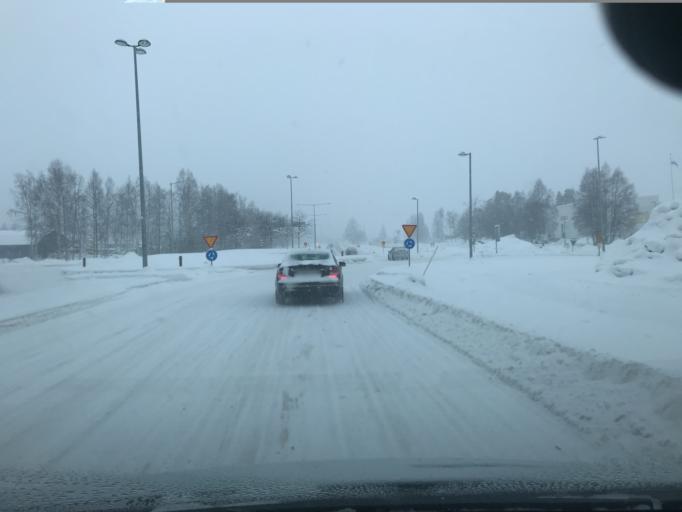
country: SE
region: Norrbotten
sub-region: Lulea Kommun
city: Lulea
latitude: 65.6134
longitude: 22.1336
